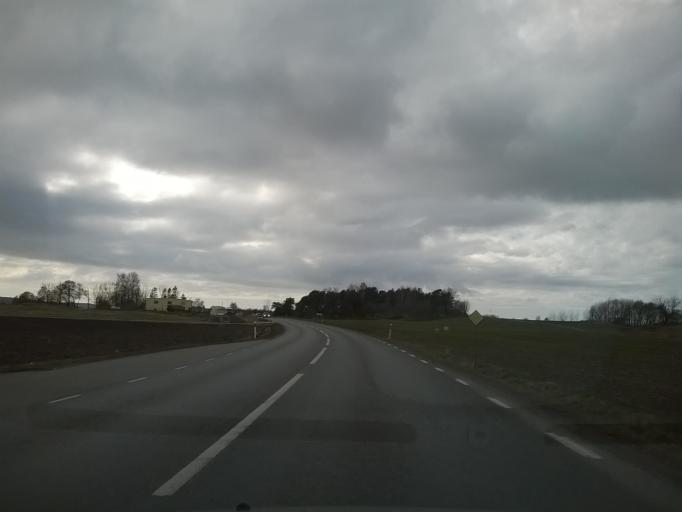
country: SE
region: Halland
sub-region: Varbergs Kommun
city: Varberg
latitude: 57.1346
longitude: 12.3273
